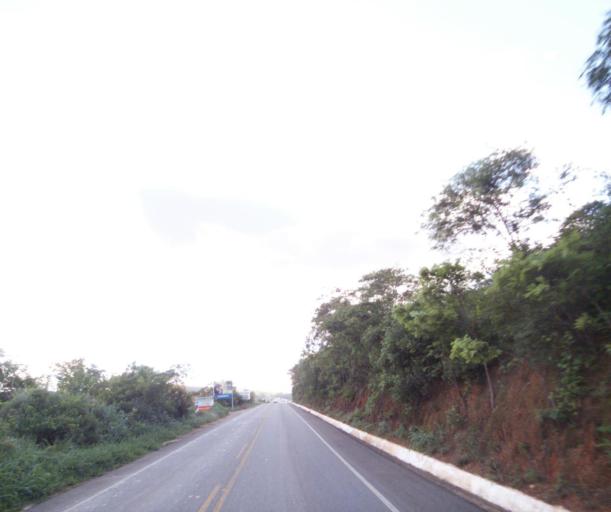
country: BR
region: Bahia
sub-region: Caetite
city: Caetite
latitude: -14.0666
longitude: -42.4708
